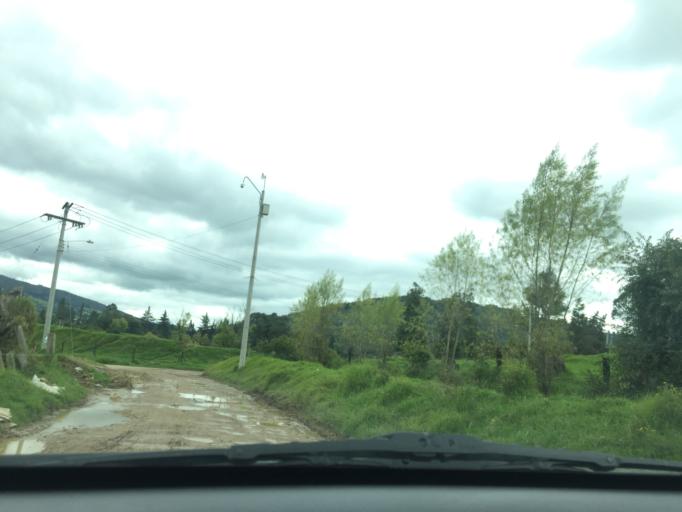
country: CO
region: Cundinamarca
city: Zipaquira
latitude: 5.0176
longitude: -73.9734
